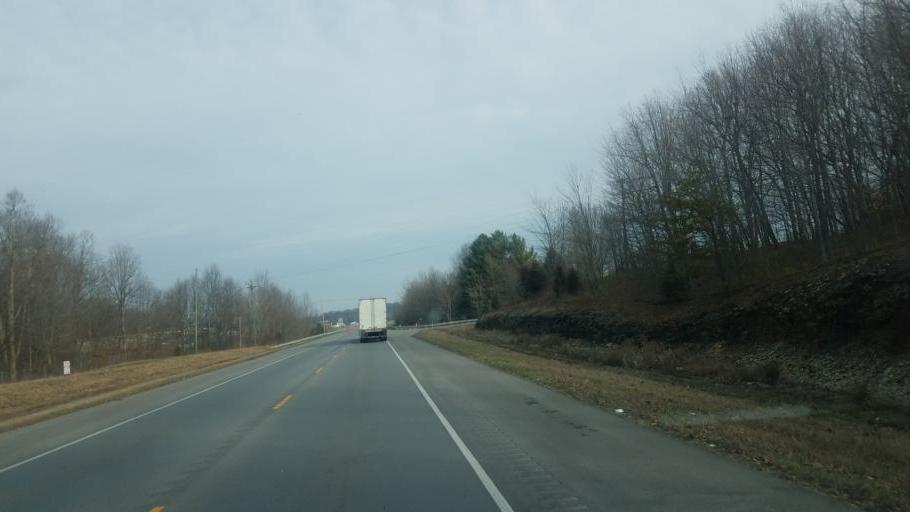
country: US
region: Kentucky
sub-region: Boyle County
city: Junction City
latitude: 37.5570
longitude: -84.7994
